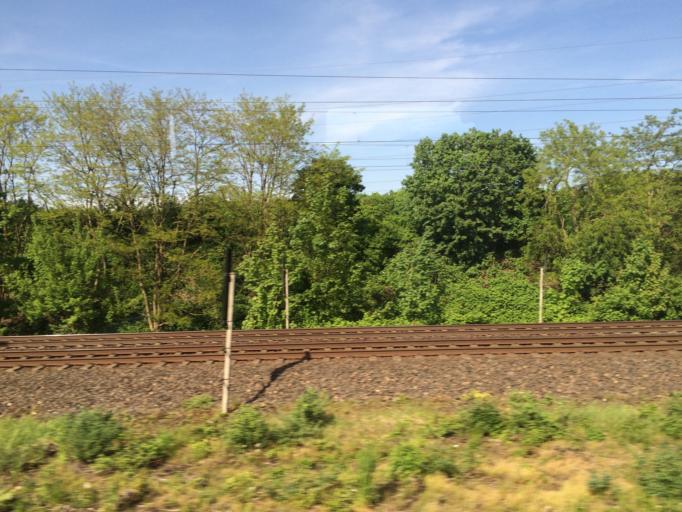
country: DE
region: North Rhine-Westphalia
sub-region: Regierungsbezirk Koln
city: Leverkusen
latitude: 51.0565
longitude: 6.9784
